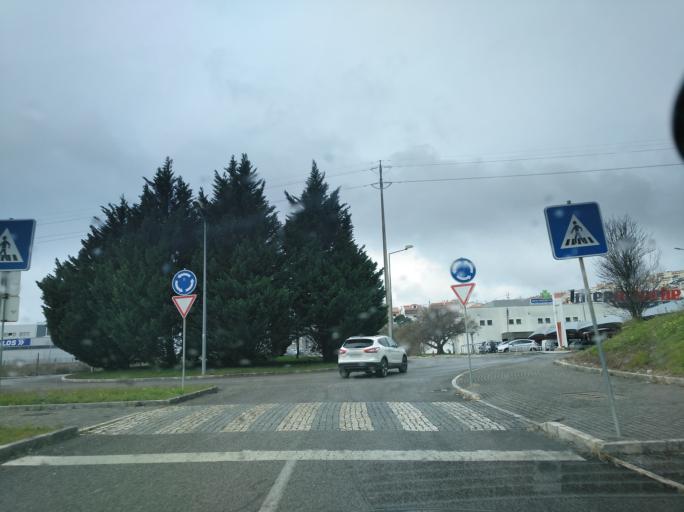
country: PT
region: Lisbon
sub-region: Odivelas
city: Famoes
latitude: 38.7913
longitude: -9.2157
